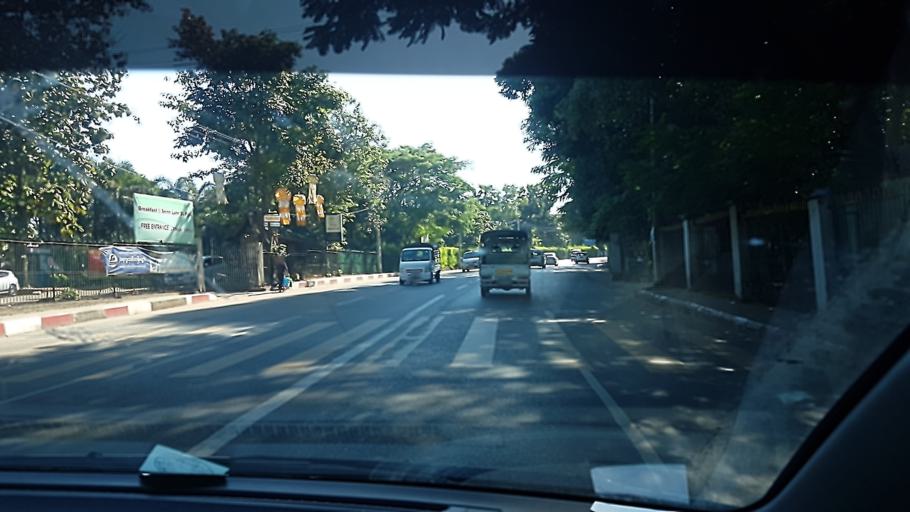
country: MM
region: Yangon
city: Yangon
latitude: 16.8338
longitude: 96.1363
